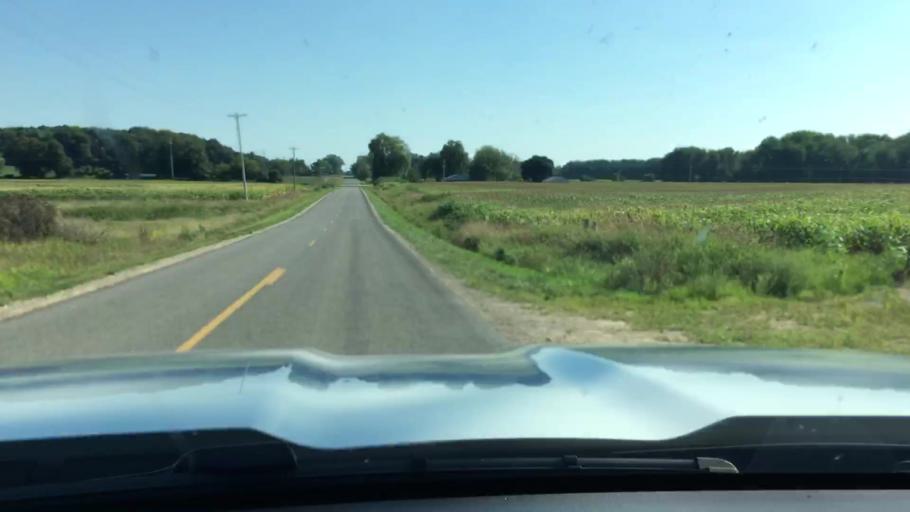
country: US
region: Michigan
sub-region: Muskegon County
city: Ravenna
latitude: 43.2537
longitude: -85.9180
